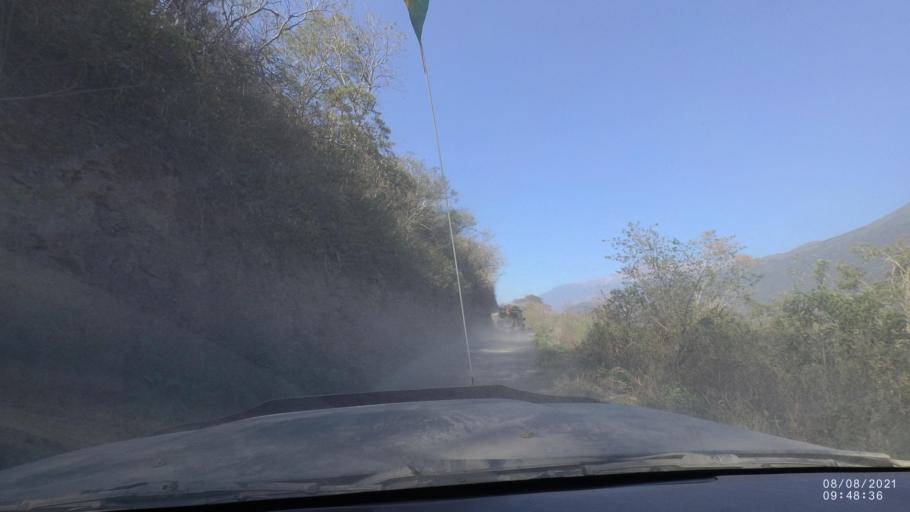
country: BO
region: La Paz
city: Quime
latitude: -16.6133
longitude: -66.7291
